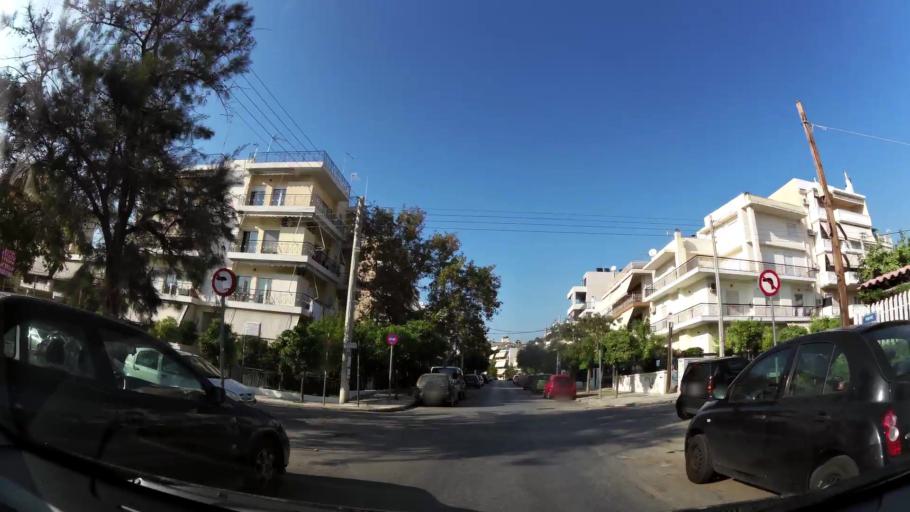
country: GR
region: Attica
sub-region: Nomarchia Athinas
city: Argyroupoli
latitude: 37.9015
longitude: 23.7538
